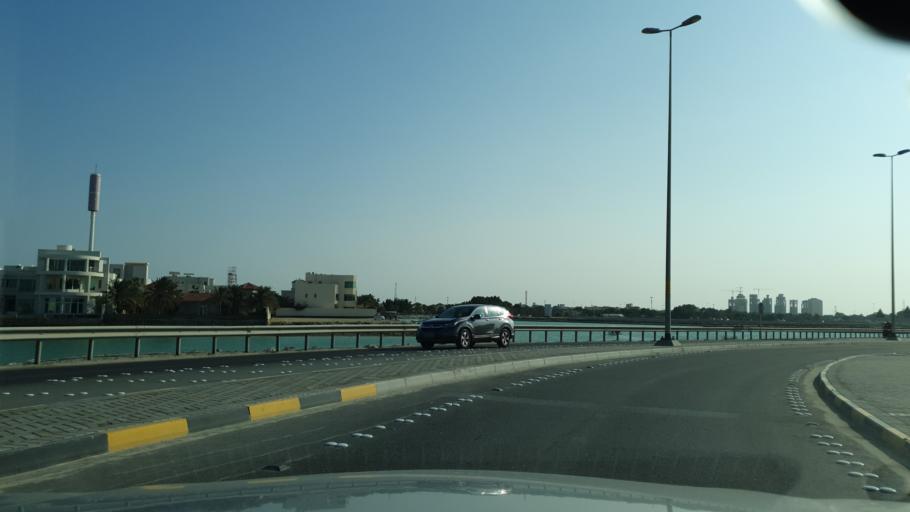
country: BH
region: Manama
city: Jidd Hafs
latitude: 26.2303
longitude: 50.4597
